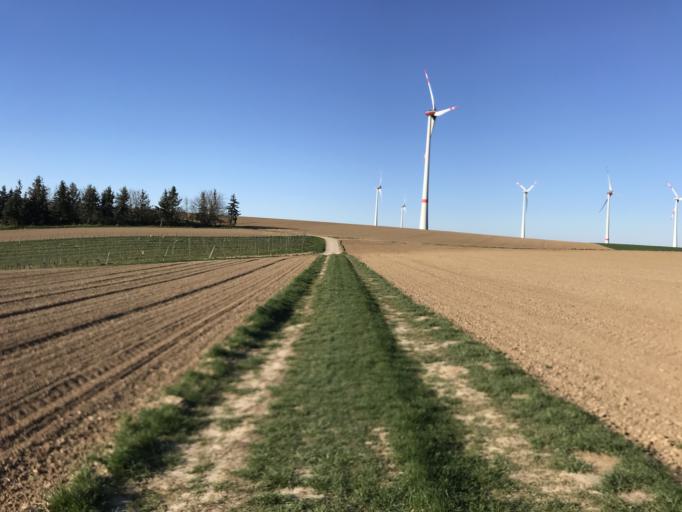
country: DE
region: Rheinland-Pfalz
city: Klein-Winternheim
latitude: 49.9302
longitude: 8.2352
